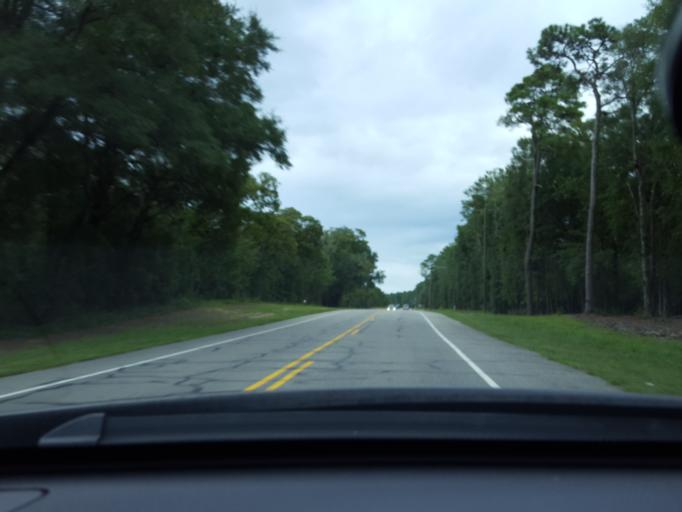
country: US
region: North Carolina
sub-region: Bladen County
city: Elizabethtown
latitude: 34.6471
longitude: -78.5184
